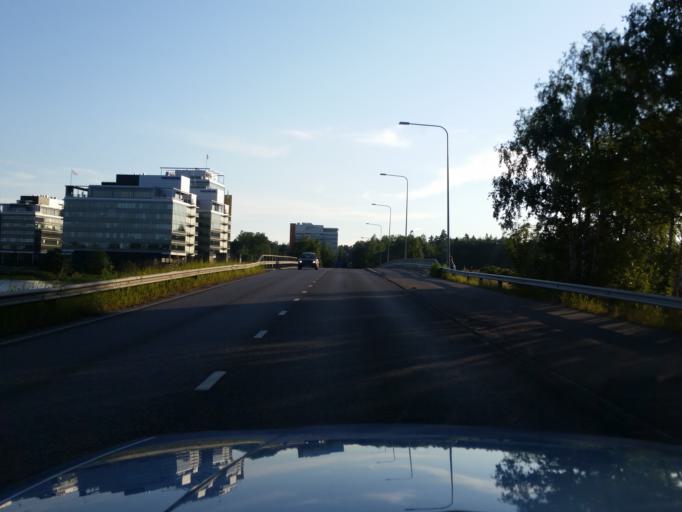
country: FI
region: Uusimaa
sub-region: Helsinki
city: Teekkarikylae
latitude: 60.1807
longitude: 24.8425
